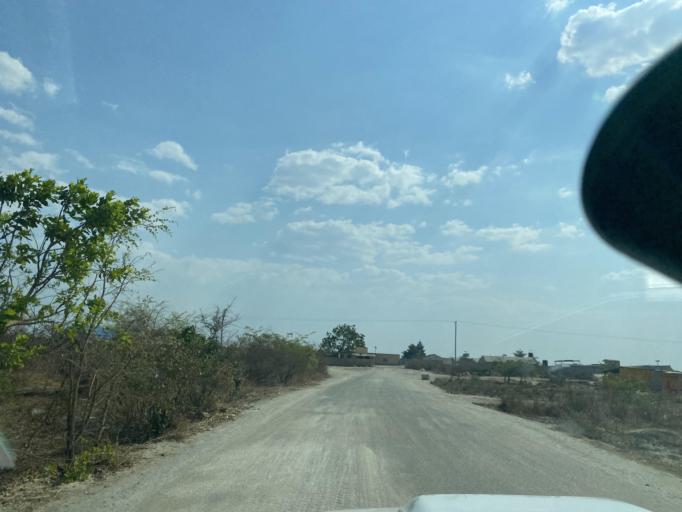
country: ZM
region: Lusaka
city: Lusaka
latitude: -15.3732
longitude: 28.0766
